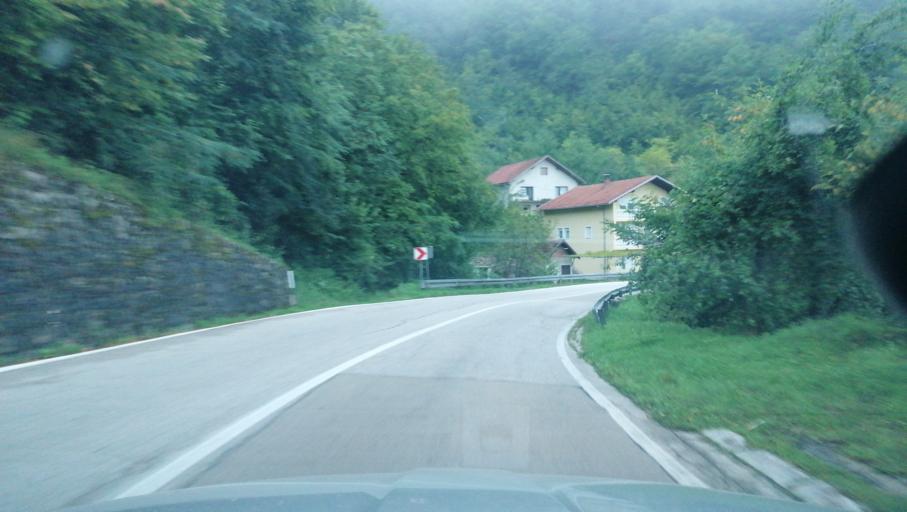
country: BA
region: Federation of Bosnia and Herzegovina
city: Jablanica
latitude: 43.7099
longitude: 17.7136
